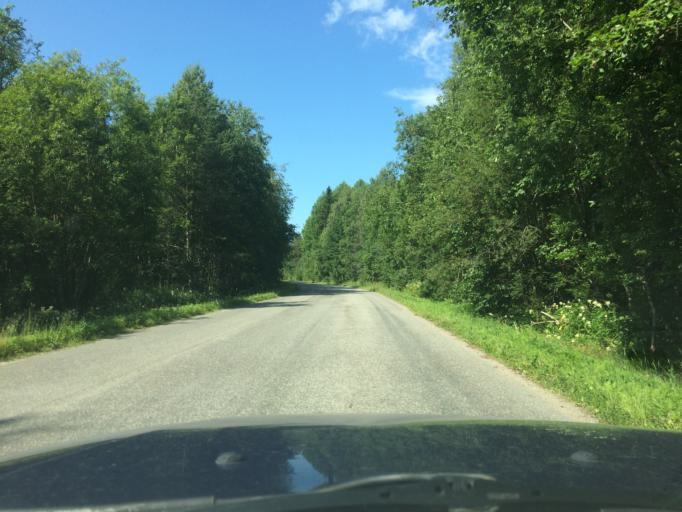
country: SE
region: Norrbotten
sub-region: Pitea Kommun
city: Norrfjarden
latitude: 65.3693
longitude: 21.4032
